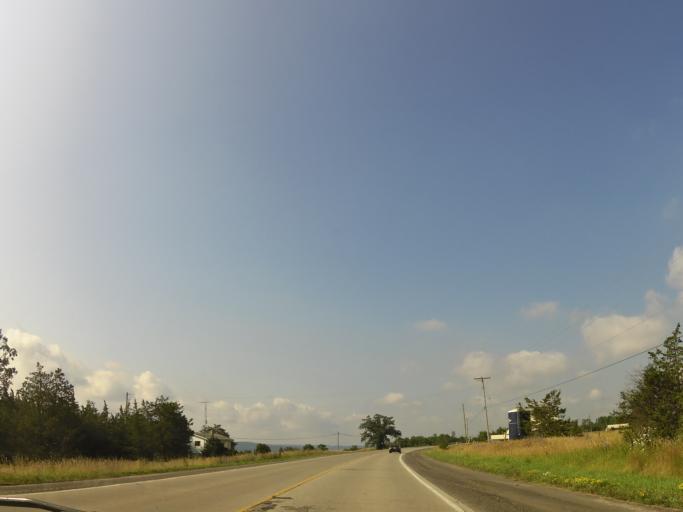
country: CA
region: Ontario
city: Picton
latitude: 44.0765
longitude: -77.0962
